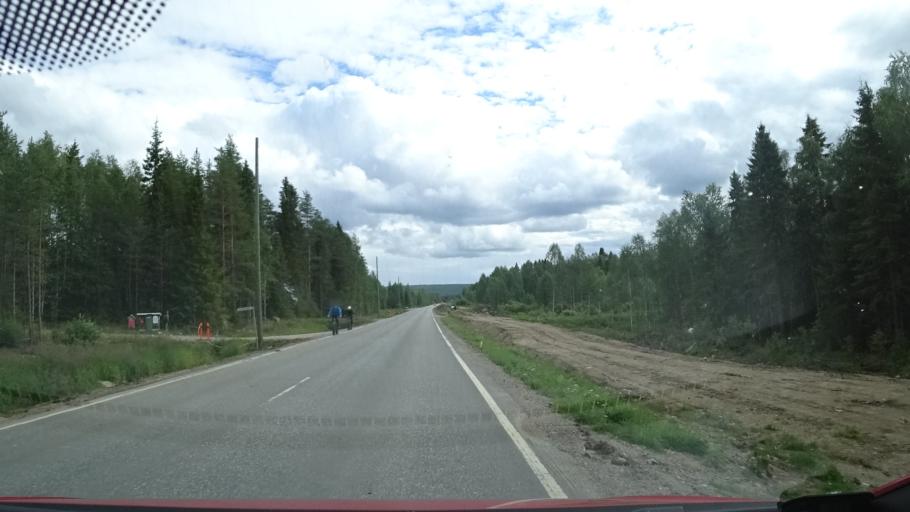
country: FI
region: Lapland
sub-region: Rovaniemi
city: Rovaniemi
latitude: 66.5315
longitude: 25.7357
